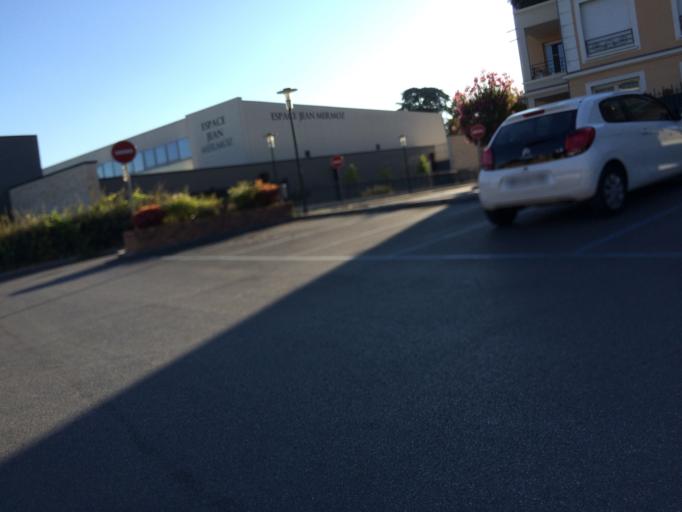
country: FR
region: Ile-de-France
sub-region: Departement de l'Essonne
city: Verrieres-le-Buisson
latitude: 48.7460
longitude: 2.2686
